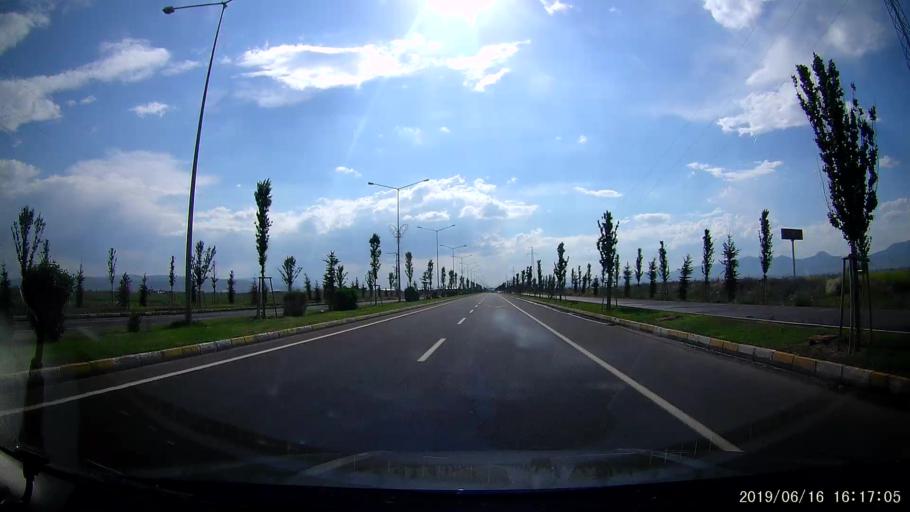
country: TR
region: Erzurum
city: Ilica
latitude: 39.9635
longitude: 41.1946
